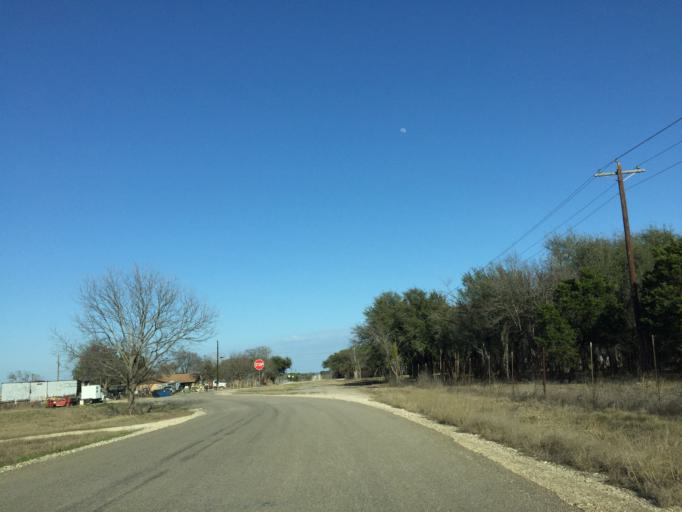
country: US
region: Texas
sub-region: Williamson County
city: Florence
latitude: 30.7645
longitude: -97.8435
